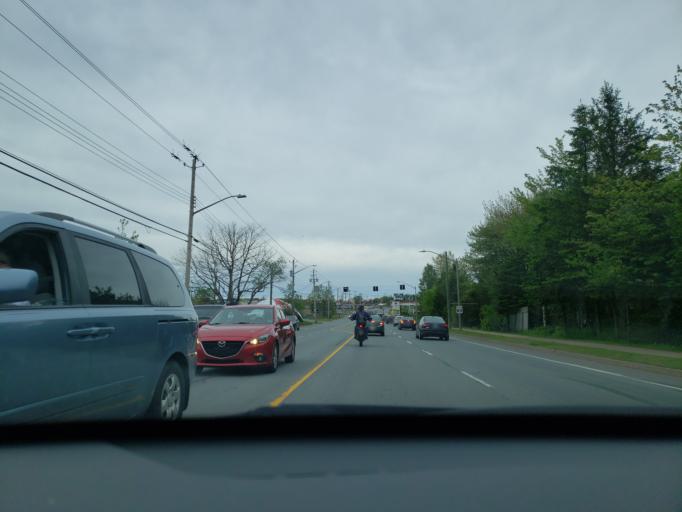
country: CA
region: Nova Scotia
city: Cole Harbour
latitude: 44.6918
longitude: -63.5042
